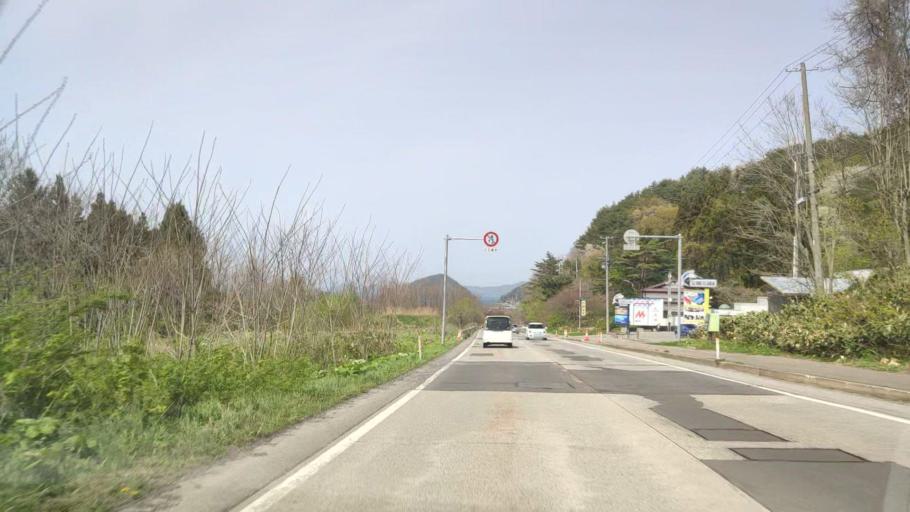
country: JP
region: Aomori
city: Aomori Shi
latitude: 40.8633
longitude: 140.8452
